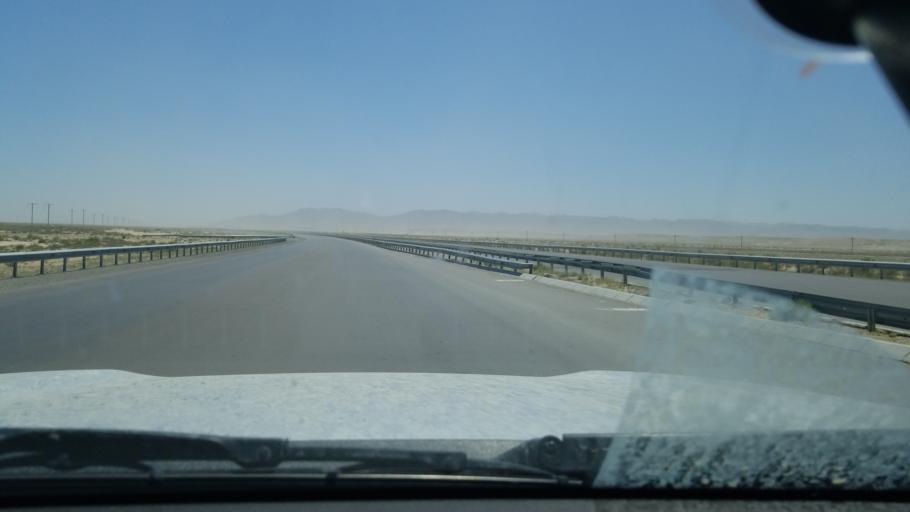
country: TM
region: Balkan
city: Gazanjyk
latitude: 39.2626
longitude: 55.3058
